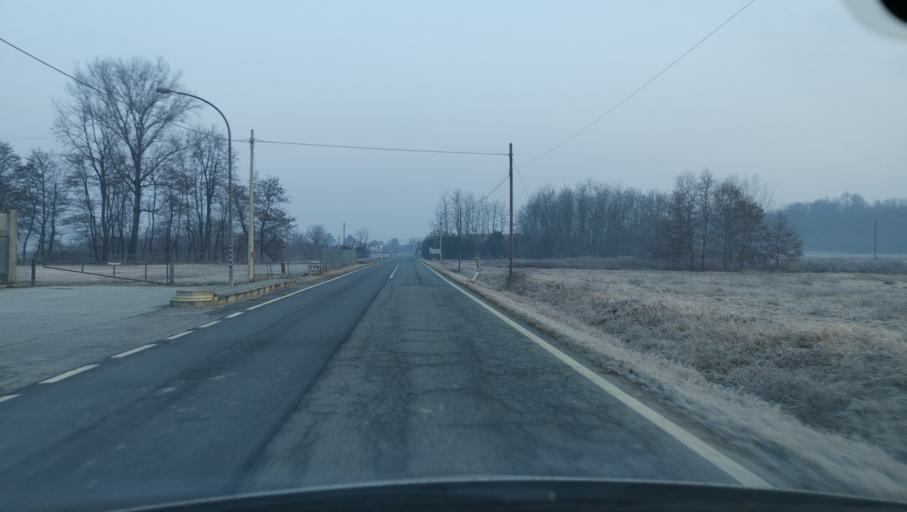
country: IT
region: Piedmont
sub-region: Provincia di Torino
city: San Giusto Canavese
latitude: 45.3004
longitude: 7.8124
